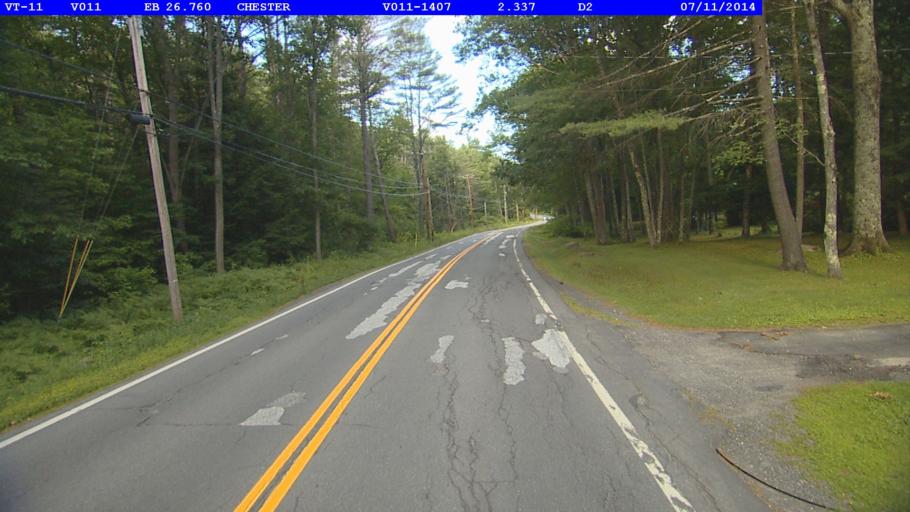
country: US
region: Vermont
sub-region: Windsor County
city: Chester
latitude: 43.2624
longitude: -72.6415
